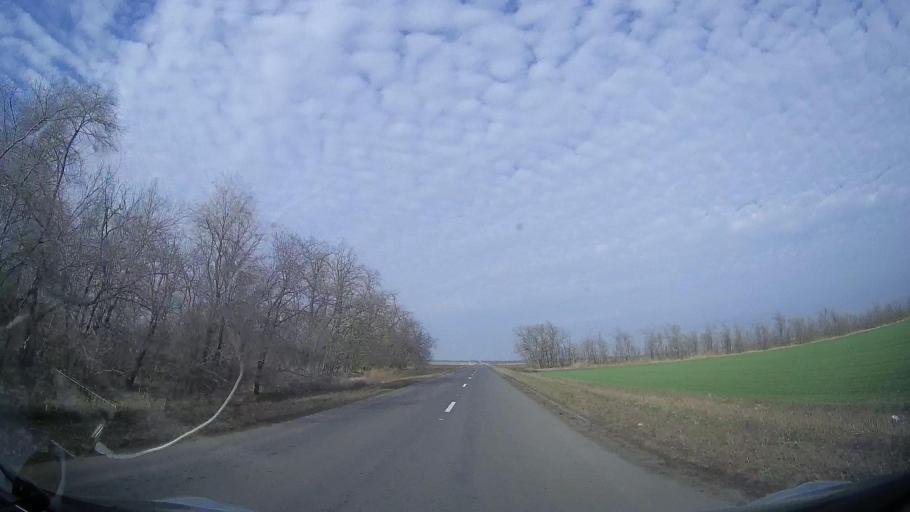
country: RU
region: Rostov
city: Gigant
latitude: 46.8764
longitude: 41.2719
